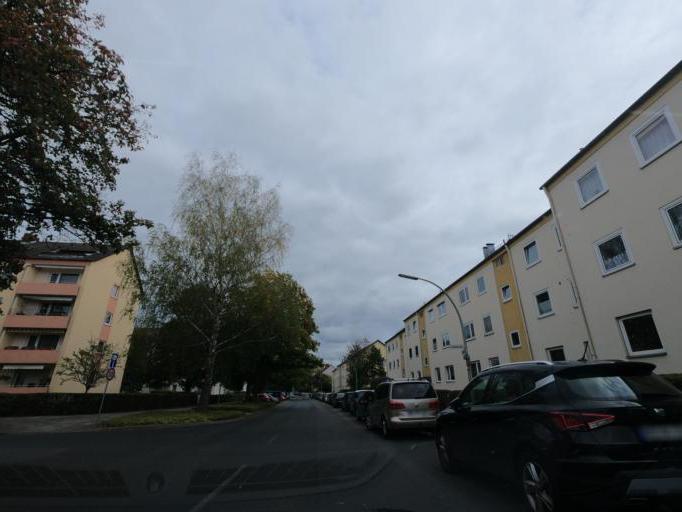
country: DE
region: Lower Saxony
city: Leiferde
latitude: 52.2417
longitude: 10.4827
